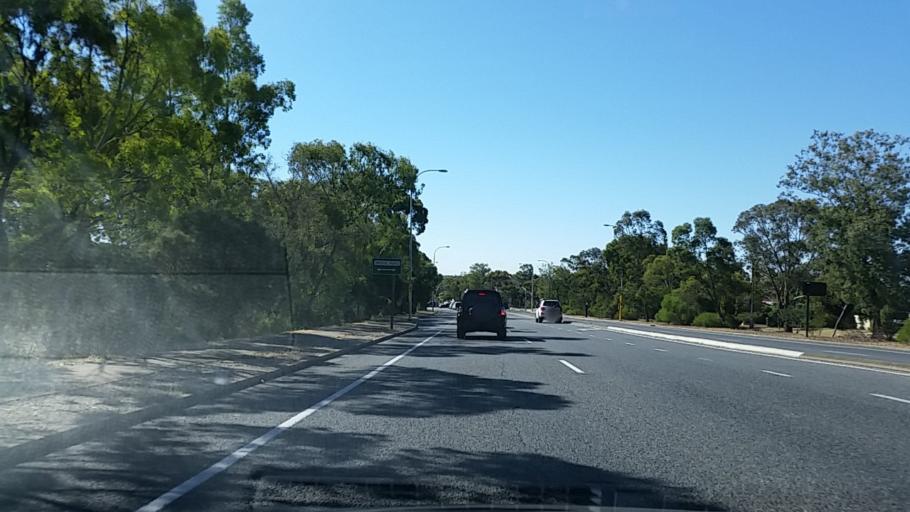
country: AU
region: South Australia
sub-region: Salisbury
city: Salisbury
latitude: -34.7995
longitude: 138.6587
